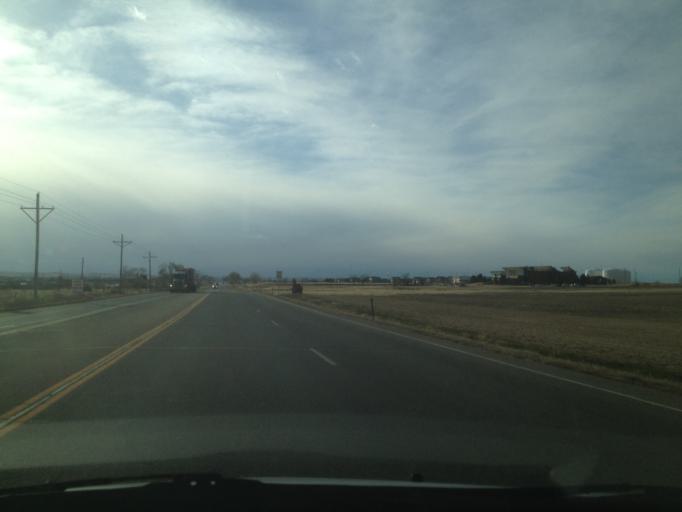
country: US
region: Colorado
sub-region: Weld County
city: Aristocrat Ranchettes
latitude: 40.0803
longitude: -104.7755
